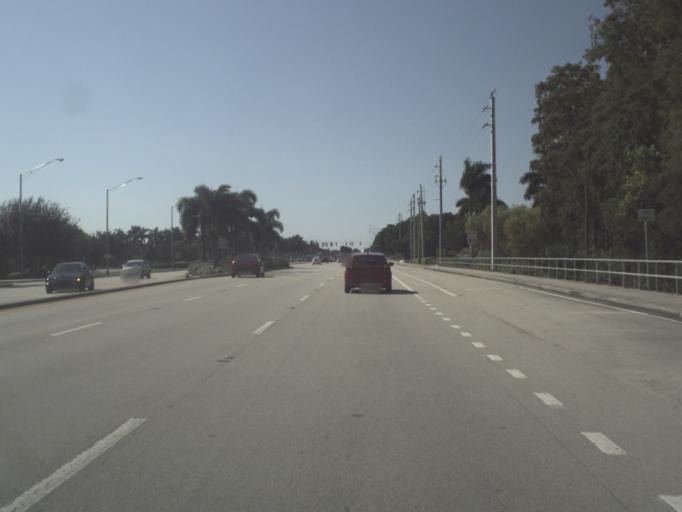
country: US
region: Florida
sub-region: Collier County
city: Naples Park
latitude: 26.2540
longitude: -81.8014
